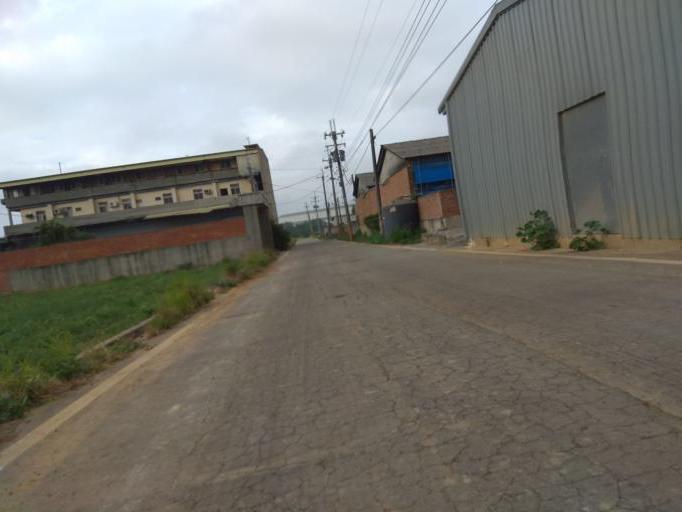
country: TW
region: Taiwan
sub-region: Hsinchu
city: Zhubei
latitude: 24.9749
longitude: 121.0401
